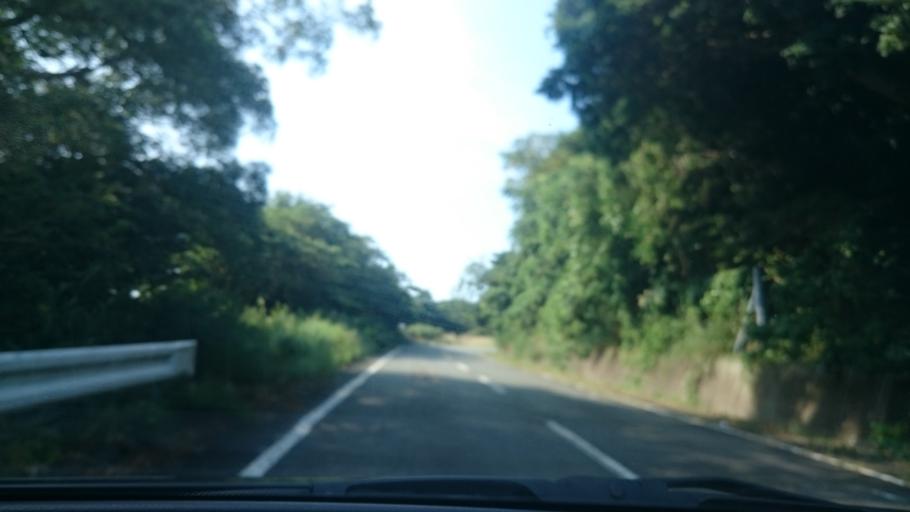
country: JP
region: Shizuoka
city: Heda
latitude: 35.0044
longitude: 138.7810
